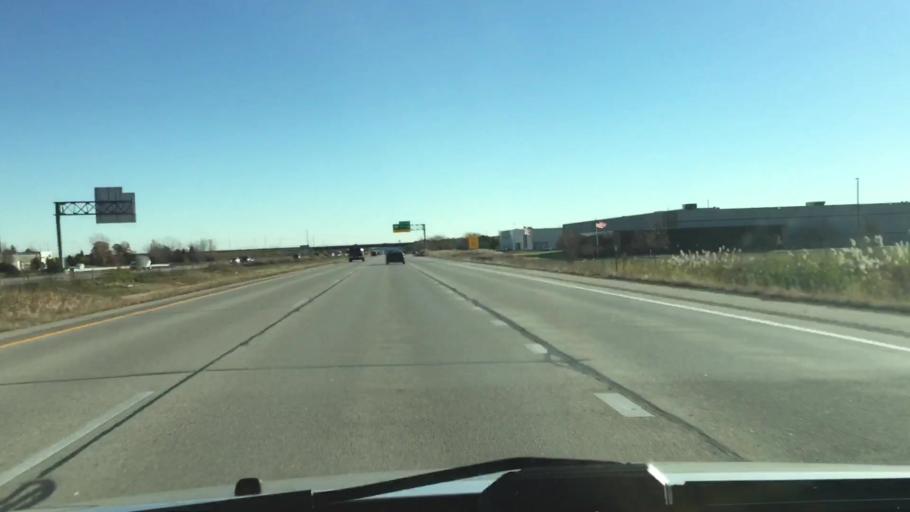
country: US
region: Wisconsin
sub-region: Outagamie County
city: Kimberly
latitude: 44.2980
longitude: -88.3649
